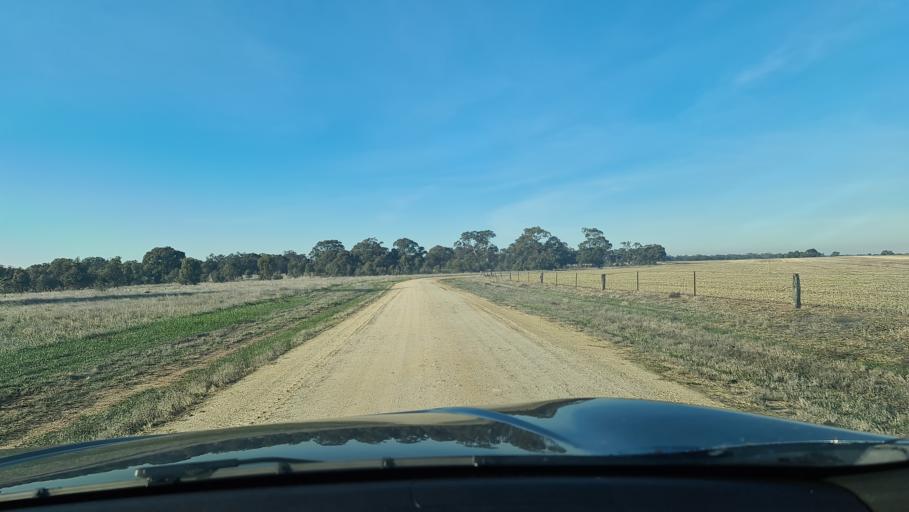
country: AU
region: Victoria
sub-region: Horsham
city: Horsham
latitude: -36.3559
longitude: 142.3957
